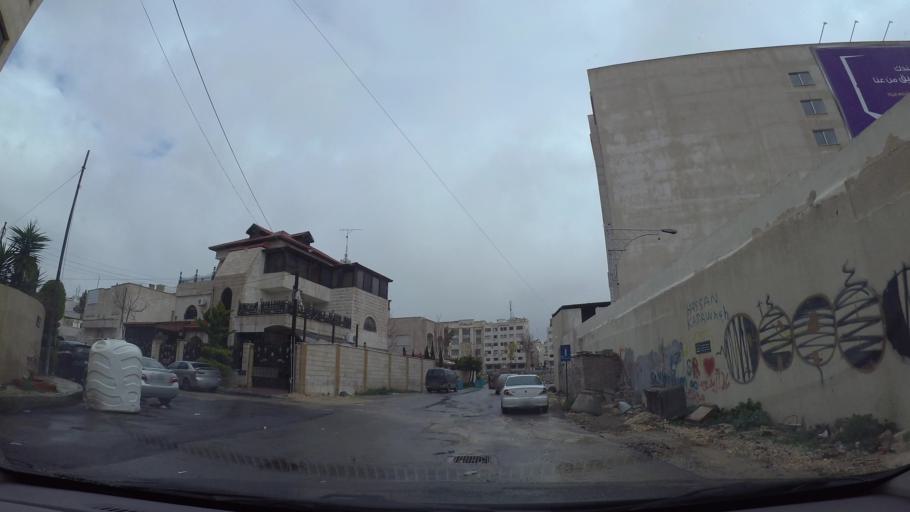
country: JO
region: Amman
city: Wadi as Sir
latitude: 31.9734
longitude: 35.8643
